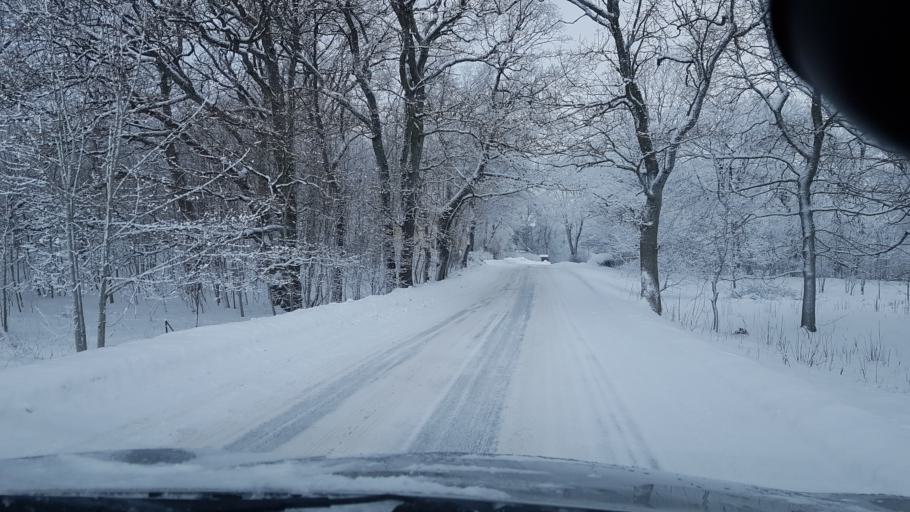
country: EE
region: Harju
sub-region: Keila linn
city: Keila
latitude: 59.3379
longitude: 24.3927
